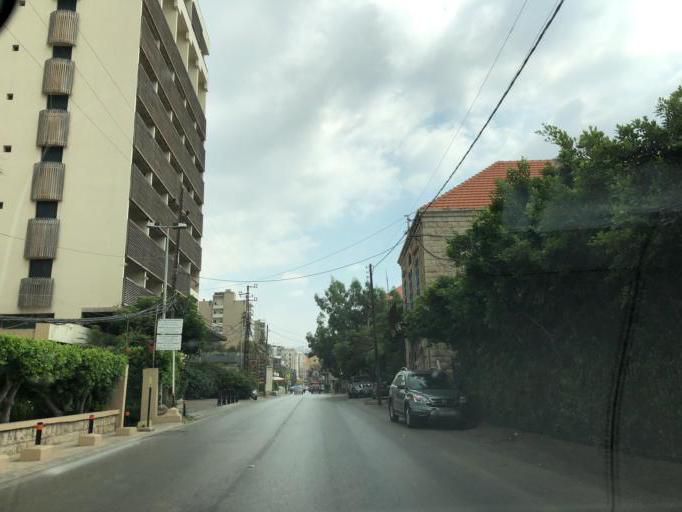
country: LB
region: Mont-Liban
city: Djounie
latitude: 33.9920
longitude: 35.6394
